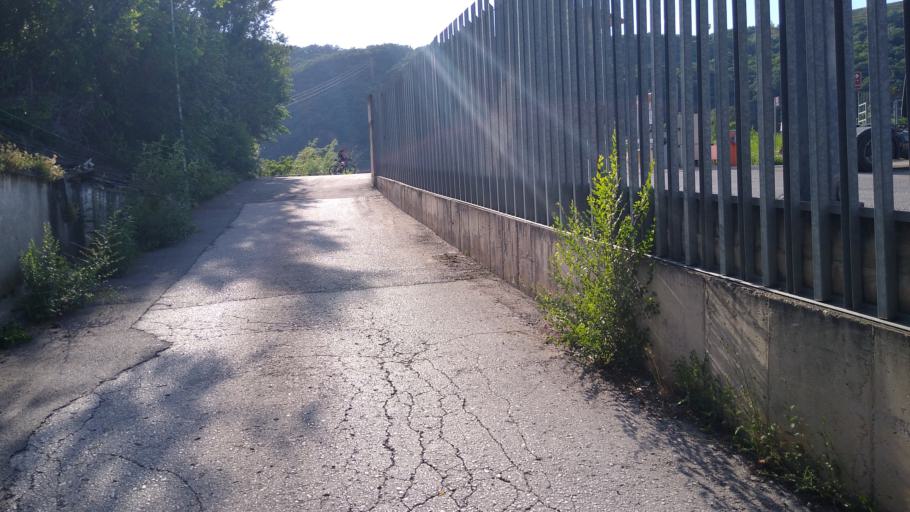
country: IT
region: Trentino-Alto Adige
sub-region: Bolzano
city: San Giacomo
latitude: 46.4704
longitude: 11.3105
